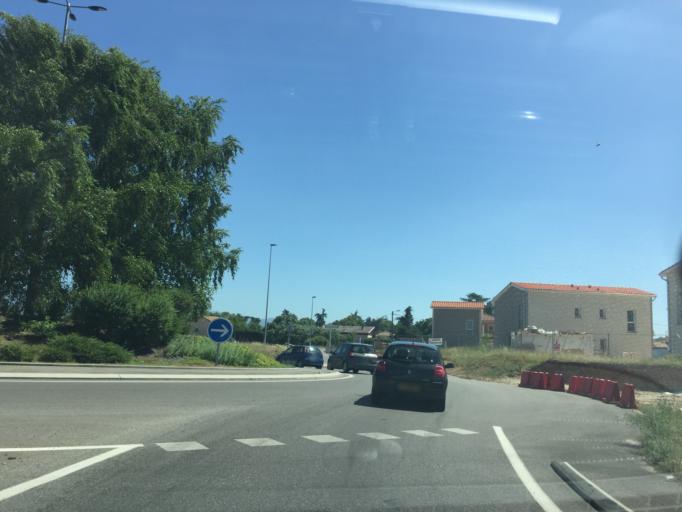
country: FR
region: Rhone-Alpes
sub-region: Departement de la Drome
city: Romans-sur-Isere
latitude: 45.0528
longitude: 5.0768
